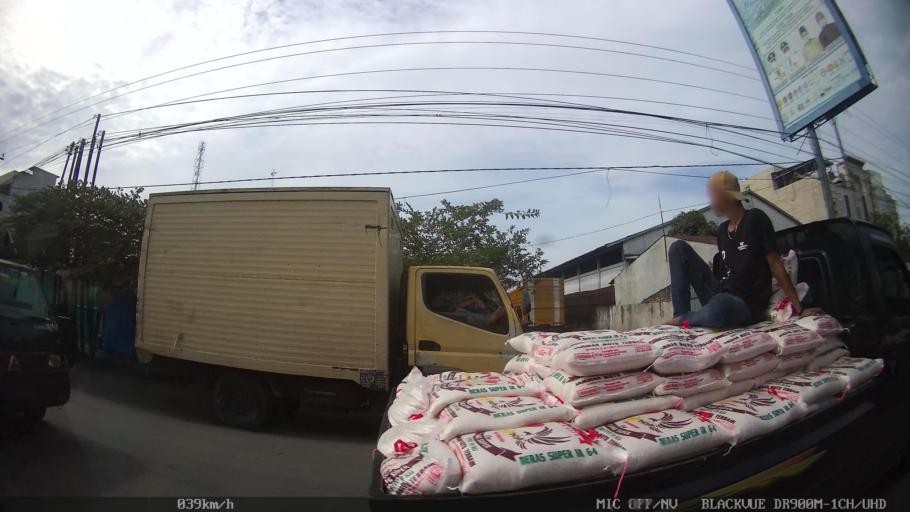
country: ID
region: North Sumatra
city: Medan
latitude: 3.6287
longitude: 98.7064
